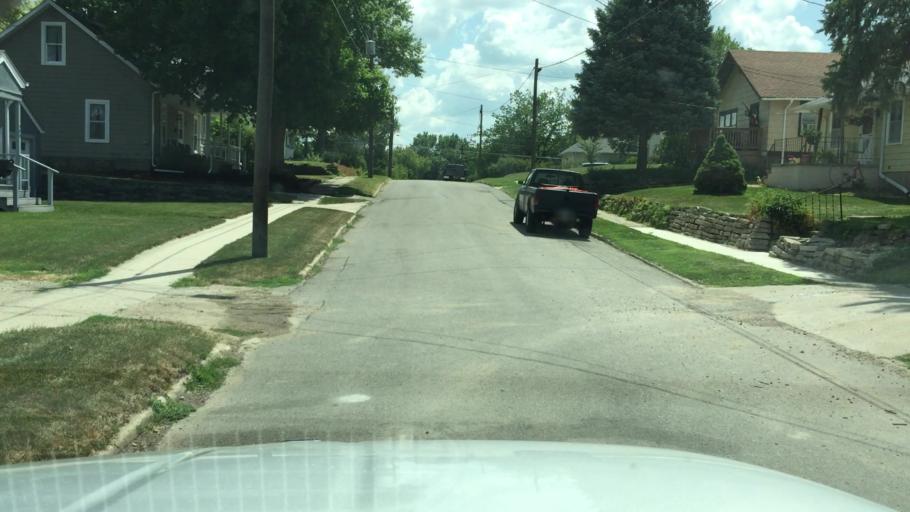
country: US
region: Iowa
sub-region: Jasper County
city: Newton
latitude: 41.6938
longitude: -93.0549
